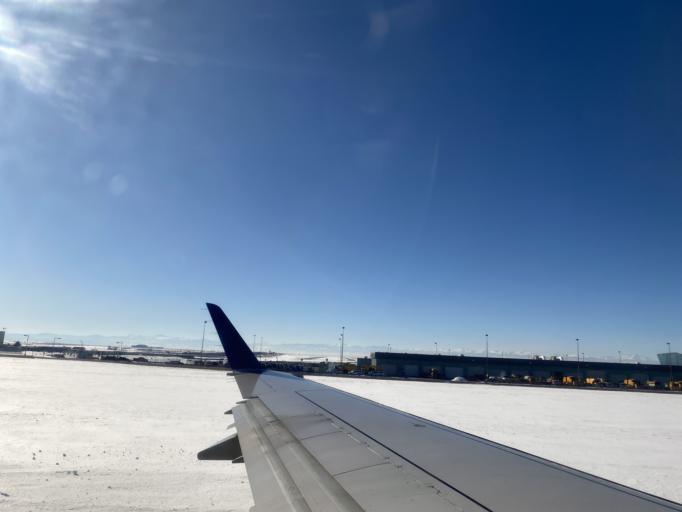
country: US
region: Colorado
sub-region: Weld County
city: Lochbuie
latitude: 39.8415
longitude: -104.6625
